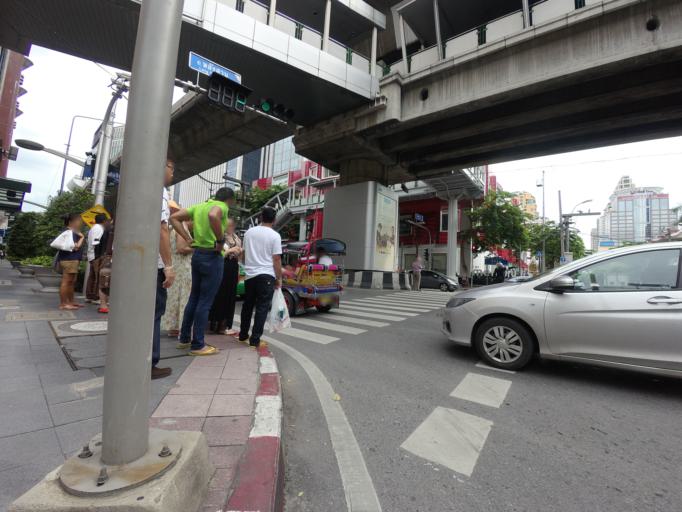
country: TH
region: Bangkok
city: Ratchathewi
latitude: 13.7436
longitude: 100.5426
